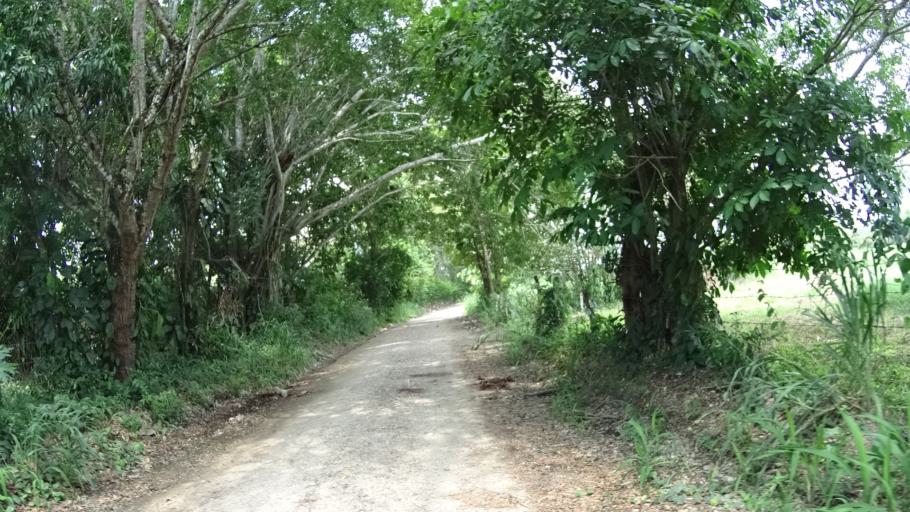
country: CO
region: Cundinamarca
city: Puerto Salgar
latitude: 5.5404
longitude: -74.6750
